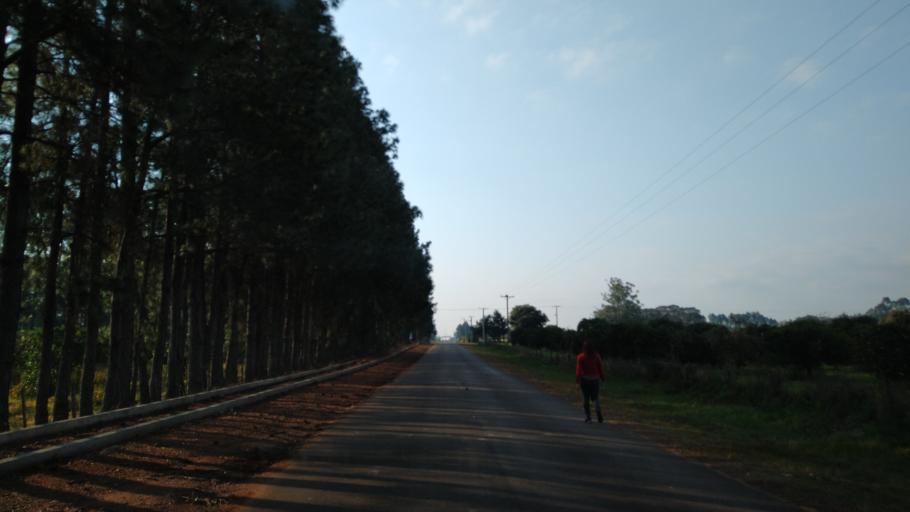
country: AR
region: Entre Rios
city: Santa Ana
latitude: -30.9061
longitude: -57.9254
